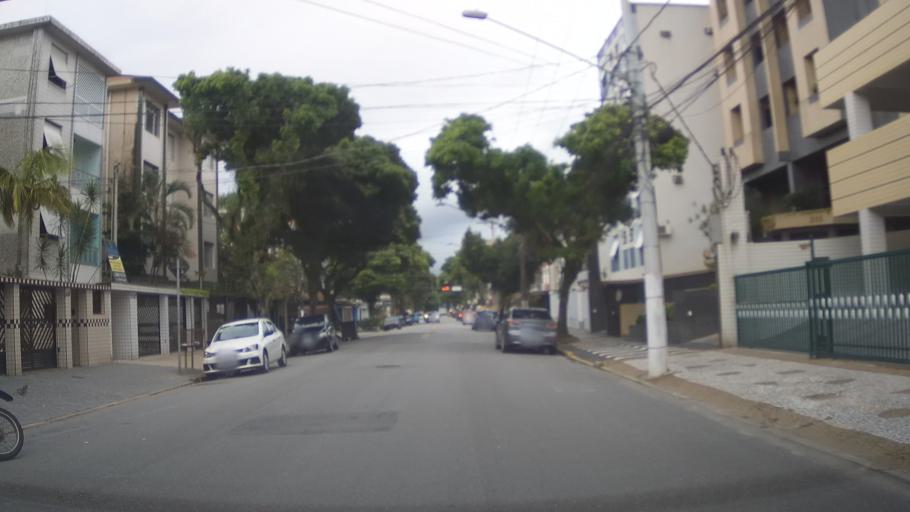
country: BR
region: Sao Paulo
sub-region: Santos
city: Santos
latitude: -23.9652
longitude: -46.3188
